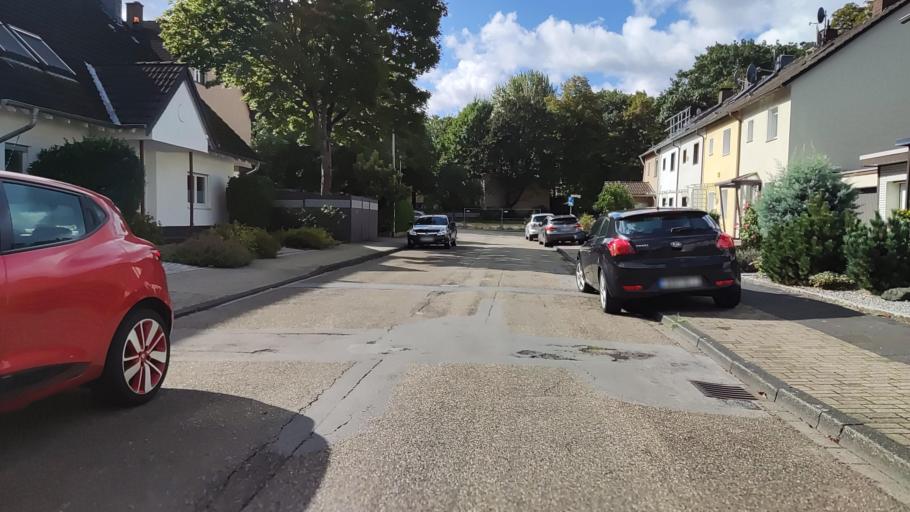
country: DE
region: North Rhine-Westphalia
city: Bochum-Hordel
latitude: 51.5209
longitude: 7.1759
